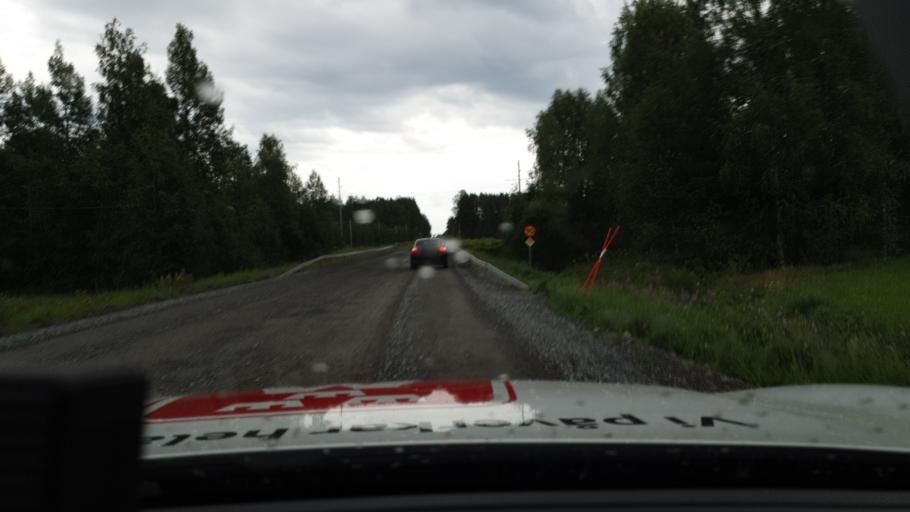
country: SE
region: Norrbotten
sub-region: Bodens Kommun
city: Boden
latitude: 65.8582
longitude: 21.4651
